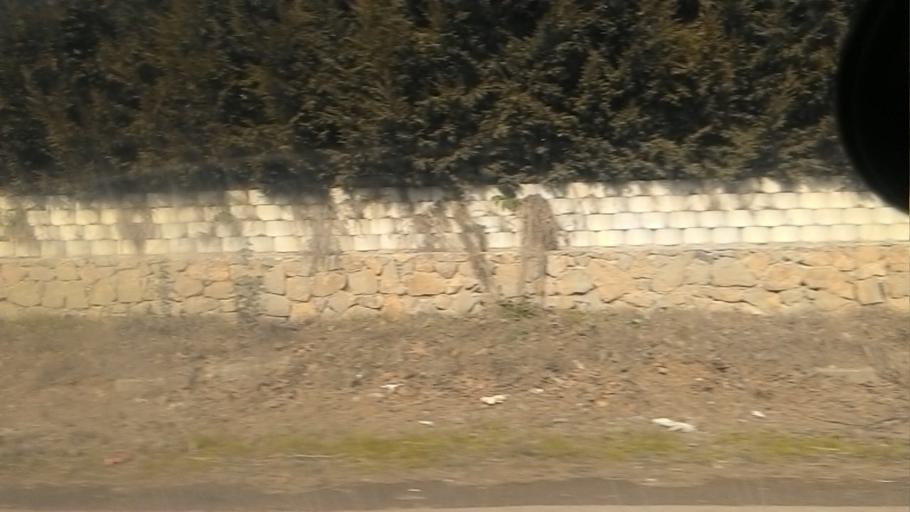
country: TR
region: Istanbul
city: Canta
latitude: 41.0765
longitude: 28.0812
